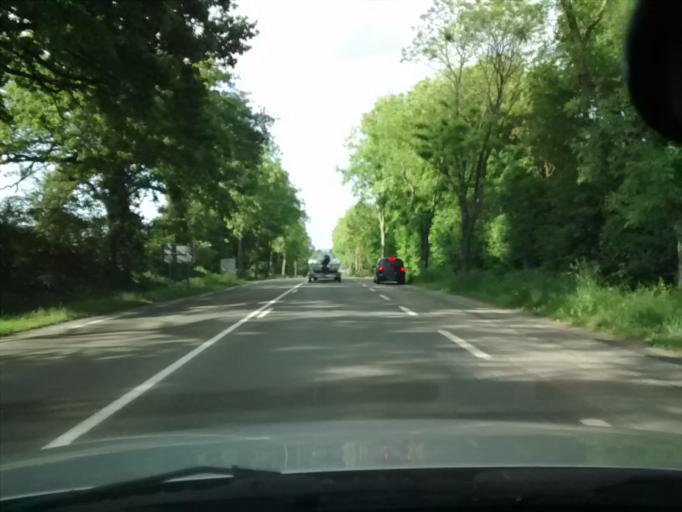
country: FR
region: Pays de la Loire
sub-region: Departement de la Mayenne
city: Chateau-Gontier
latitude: 47.8427
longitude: -0.6976
